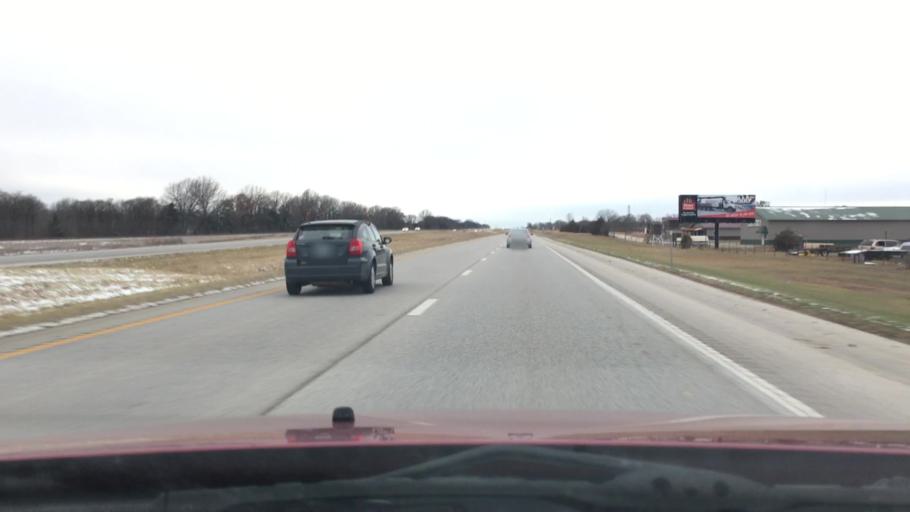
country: US
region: Missouri
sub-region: Webster County
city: Seymour
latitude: 37.1696
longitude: -92.8274
